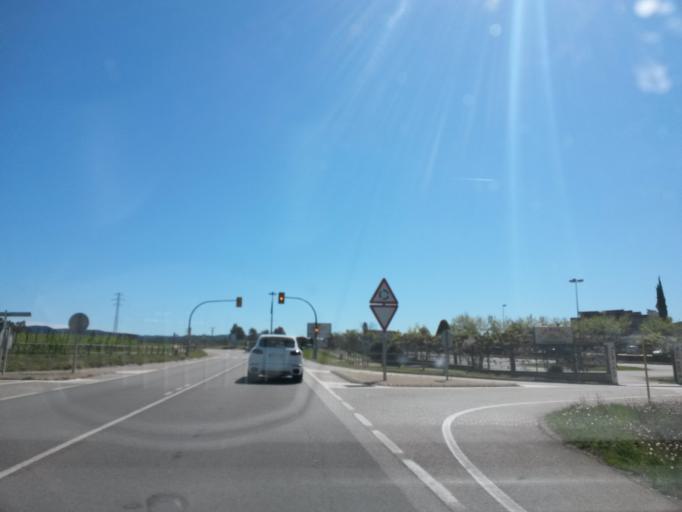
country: ES
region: Catalonia
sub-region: Provincia de Girona
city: Riudellots de la Selva
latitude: 41.8967
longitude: 2.8301
